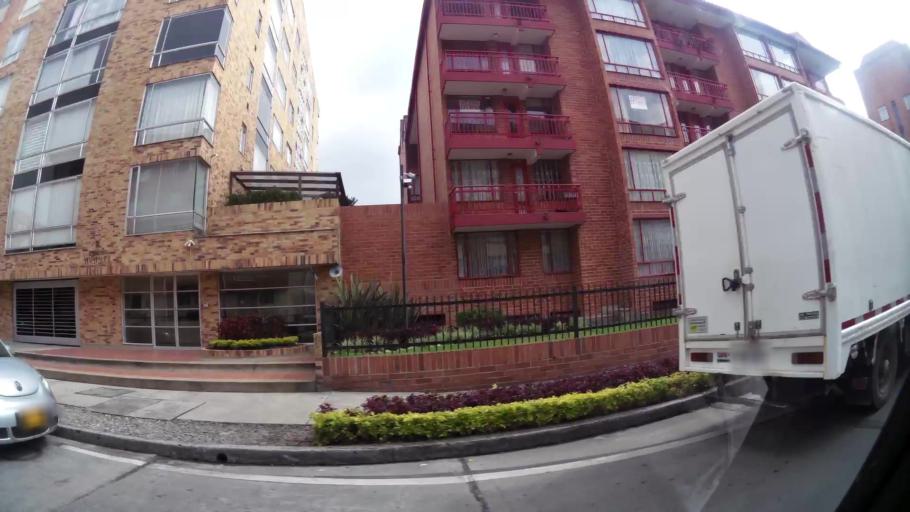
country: CO
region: Bogota D.C.
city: Barrio San Luis
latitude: 4.7316
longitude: -74.0521
